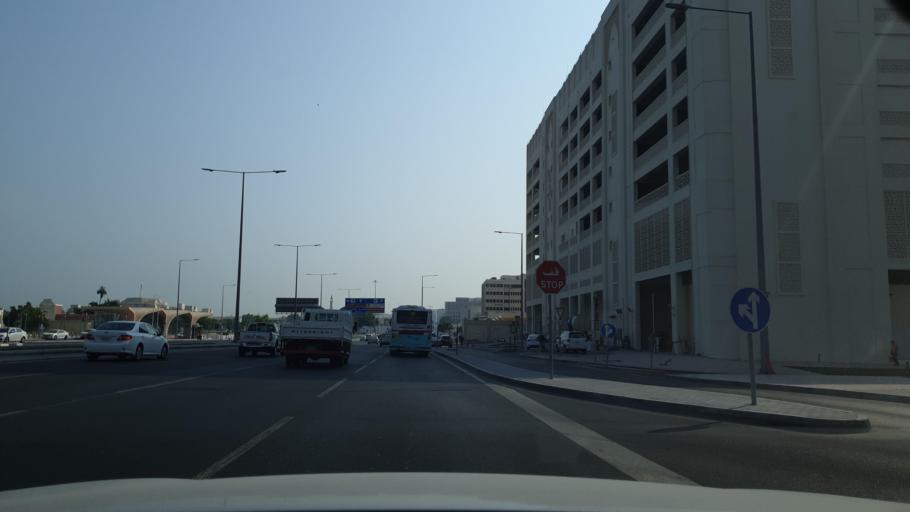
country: QA
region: Baladiyat ad Dawhah
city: Doha
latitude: 25.2891
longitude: 51.5189
